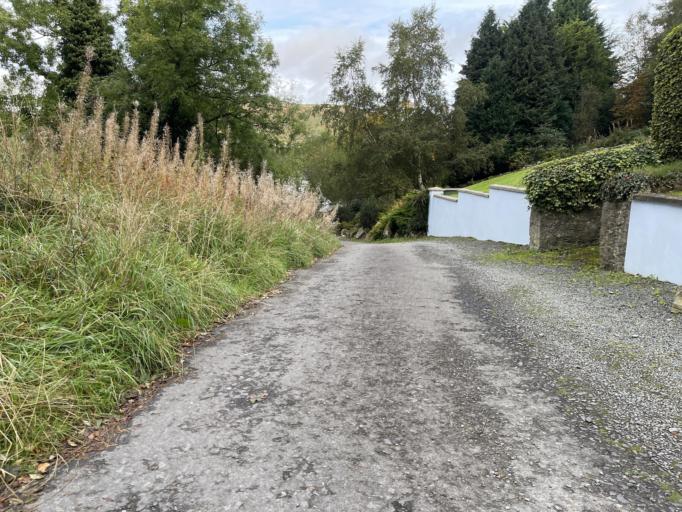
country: GB
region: Northern Ireland
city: Rostrevor
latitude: 54.1076
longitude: -6.1786
